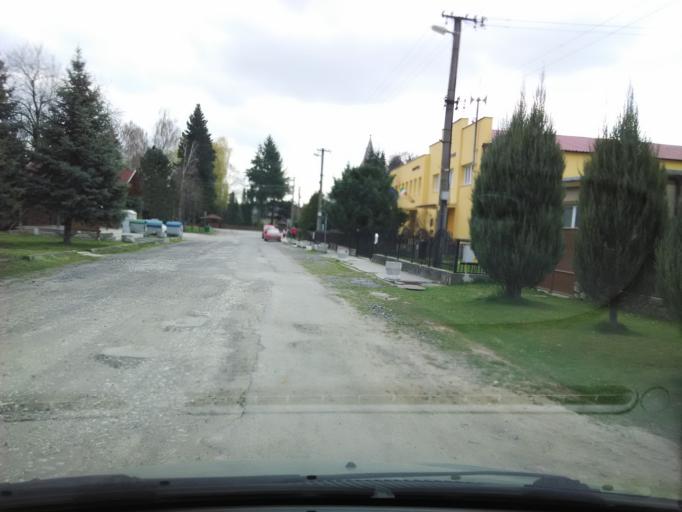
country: SK
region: Nitriansky
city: Zlate Moravce
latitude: 48.4187
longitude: 18.3559
